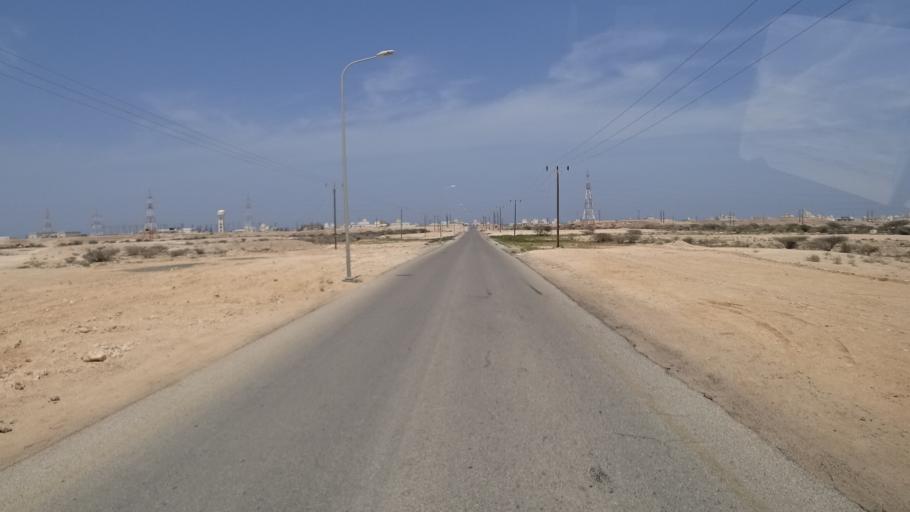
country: OM
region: Ash Sharqiyah
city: Sur
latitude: 22.6119
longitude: 59.4522
